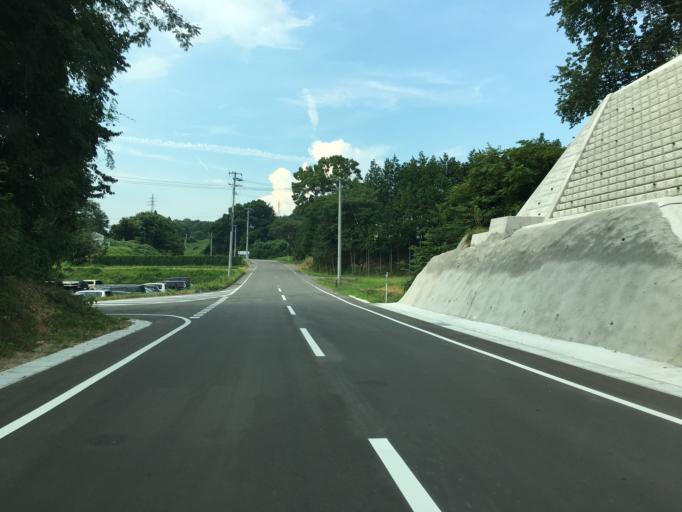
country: JP
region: Fukushima
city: Motomiya
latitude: 37.4855
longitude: 140.4129
